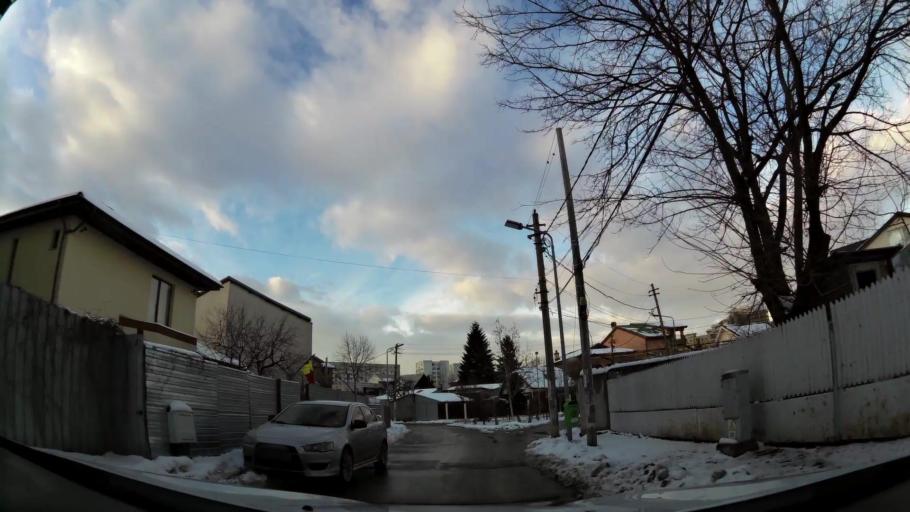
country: RO
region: Ilfov
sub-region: Comuna Popesti-Leordeni
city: Popesti-Leordeni
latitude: 44.3778
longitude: 26.1305
